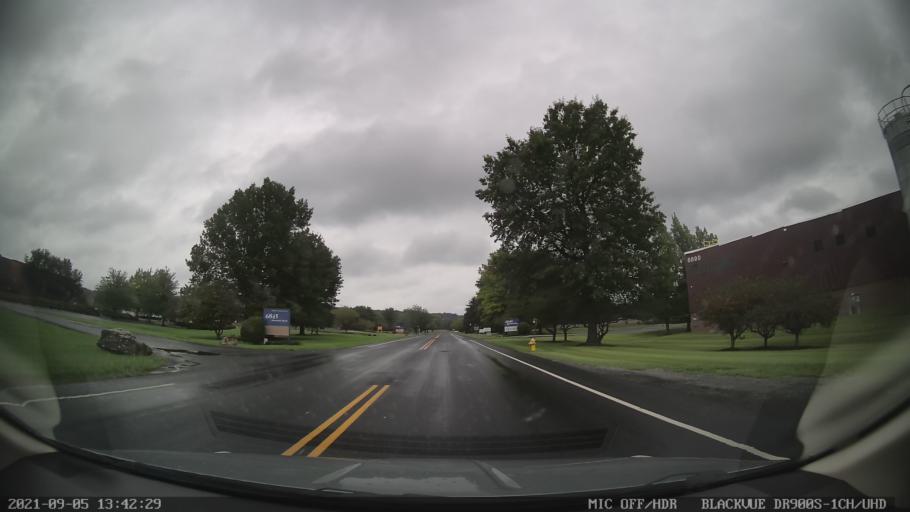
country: US
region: Pennsylvania
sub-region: Lehigh County
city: Trexlertown
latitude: 40.5911
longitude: -75.6097
